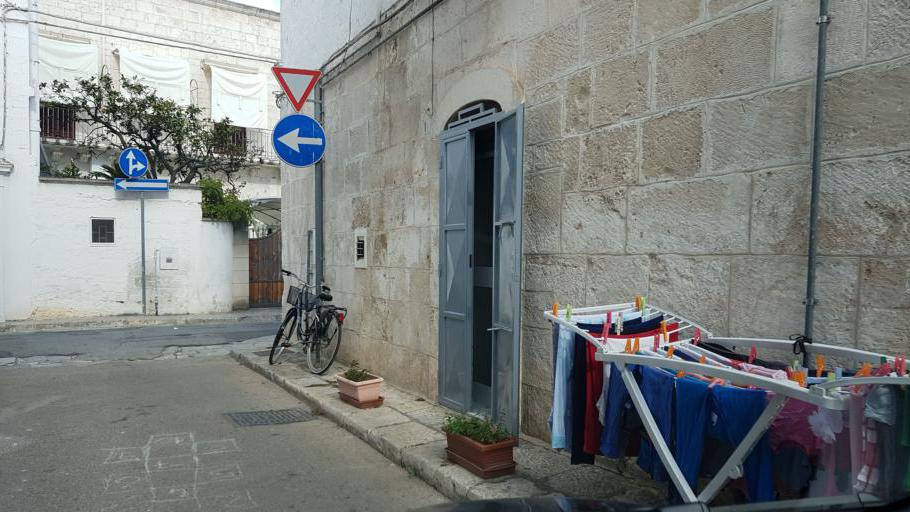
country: IT
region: Apulia
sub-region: Provincia di Brindisi
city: Ostuni
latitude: 40.7289
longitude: 17.5757
